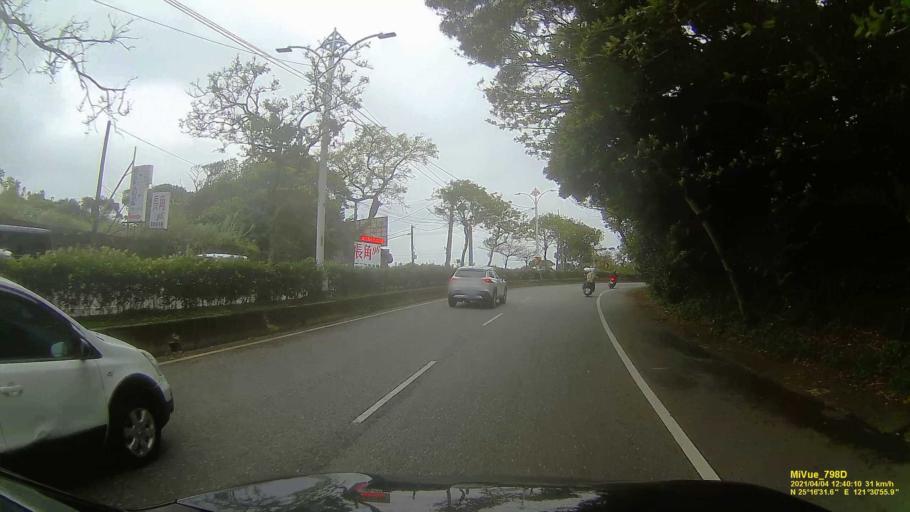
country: TW
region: Taipei
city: Taipei
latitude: 25.2754
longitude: 121.5155
